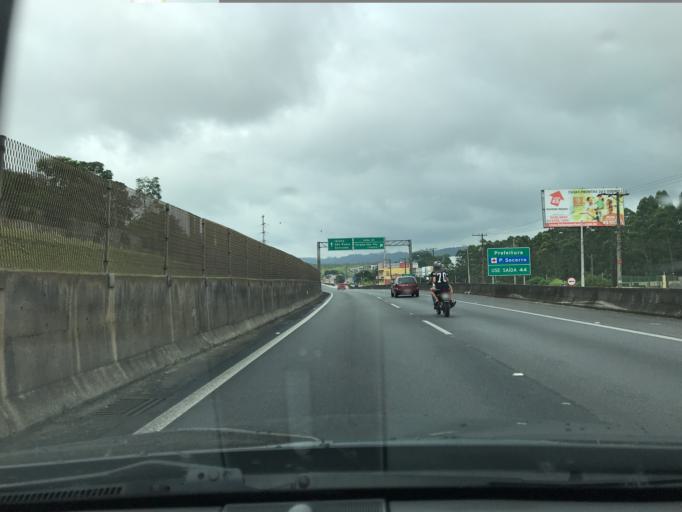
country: BR
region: Sao Paulo
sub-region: Vargem Grande Paulista
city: Vargem Grande Paulista
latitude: -23.6077
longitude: -47.0107
